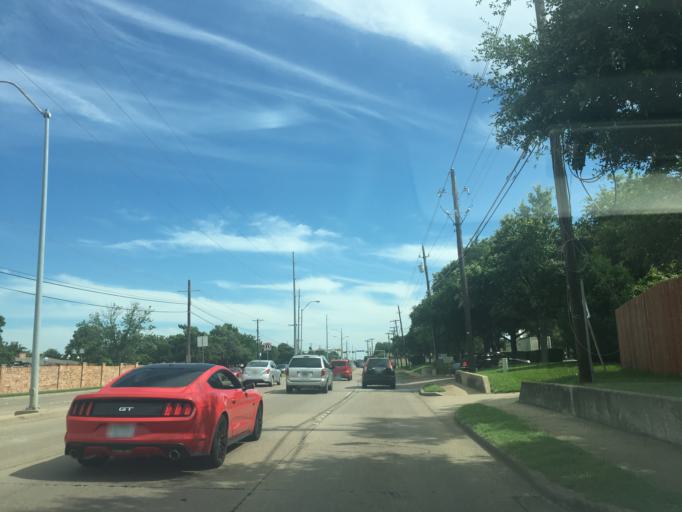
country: US
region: Texas
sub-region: Dallas County
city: Richardson
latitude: 32.9404
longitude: -96.6830
